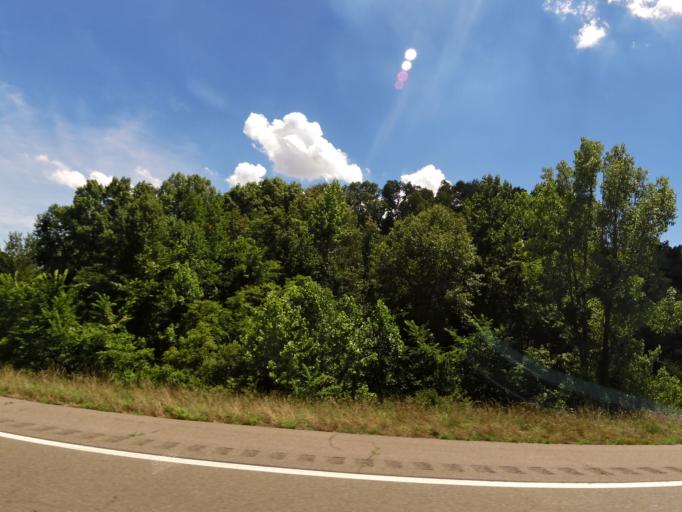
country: US
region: Tennessee
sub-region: Dyer County
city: Dyersburg
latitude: 36.0733
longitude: -89.4790
